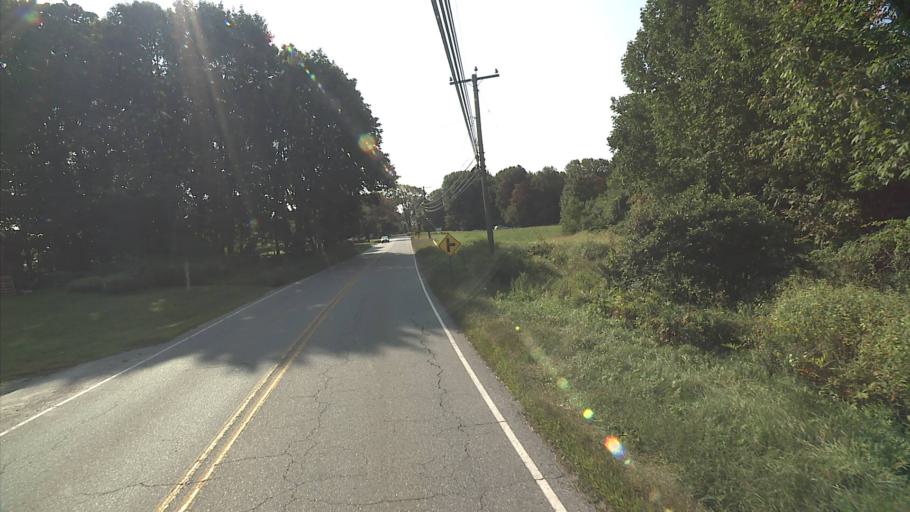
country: US
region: Connecticut
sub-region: Windham County
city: South Windham
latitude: 41.6282
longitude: -72.1998
